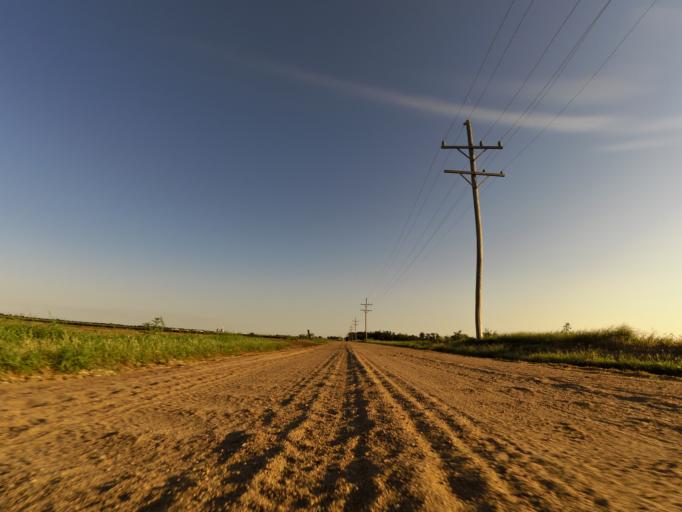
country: US
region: Kansas
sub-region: Reno County
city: South Hutchinson
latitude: 38.0106
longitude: -98.0320
